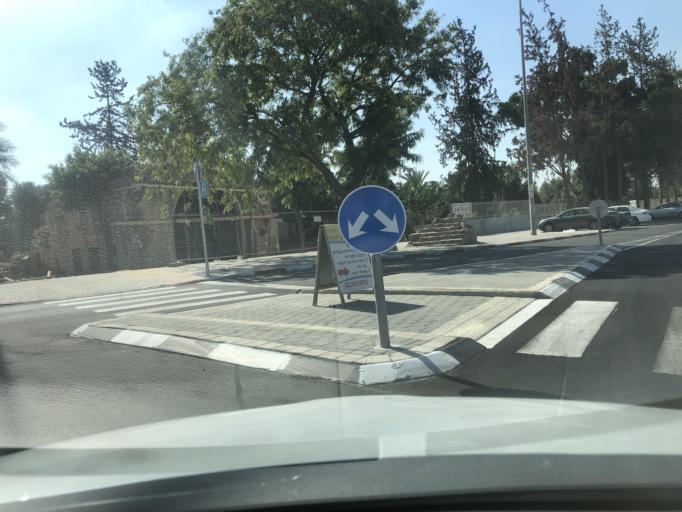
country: IL
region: Central District
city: Jaljulya
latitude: 32.1532
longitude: 34.9488
